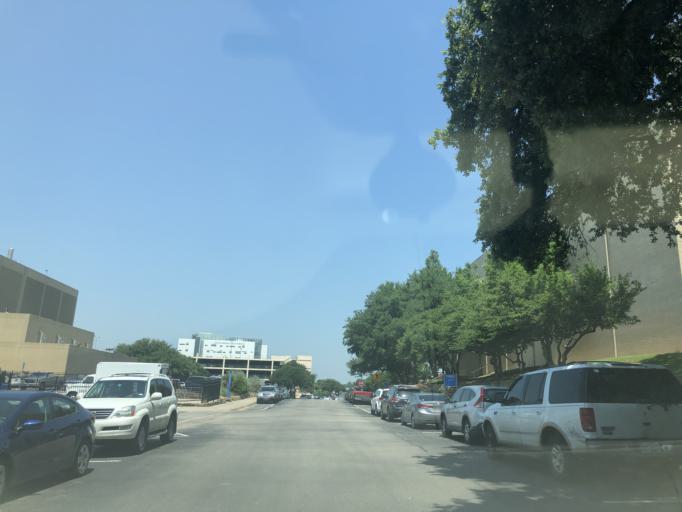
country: US
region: Texas
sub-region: Dallas County
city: Dallas
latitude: 32.8114
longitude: -96.8420
